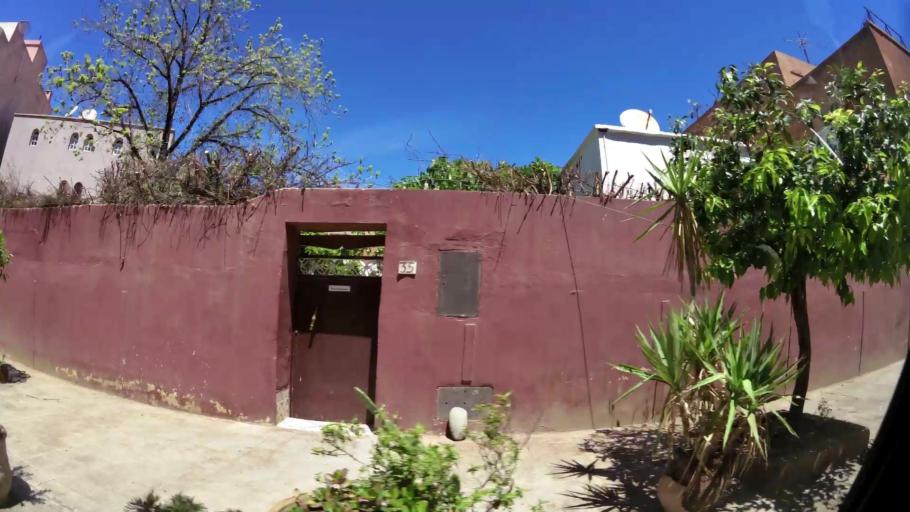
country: MA
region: Marrakech-Tensift-Al Haouz
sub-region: Marrakech
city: Marrakesh
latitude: 31.6275
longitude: -8.0169
